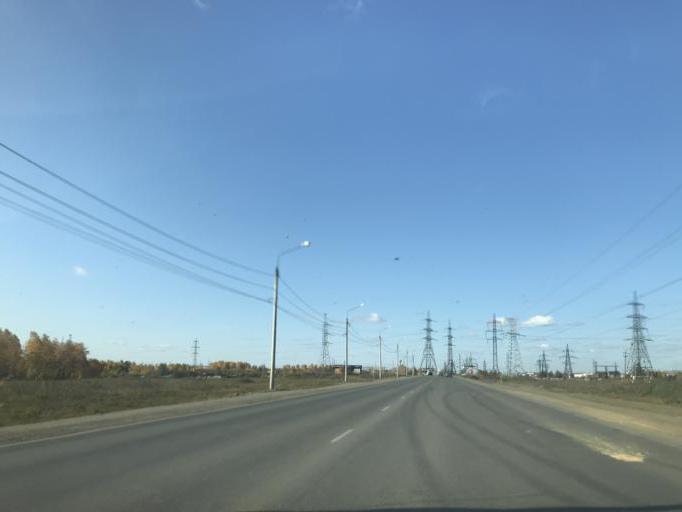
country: RU
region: Chelyabinsk
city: Roshchino
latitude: 55.2228
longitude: 61.2938
